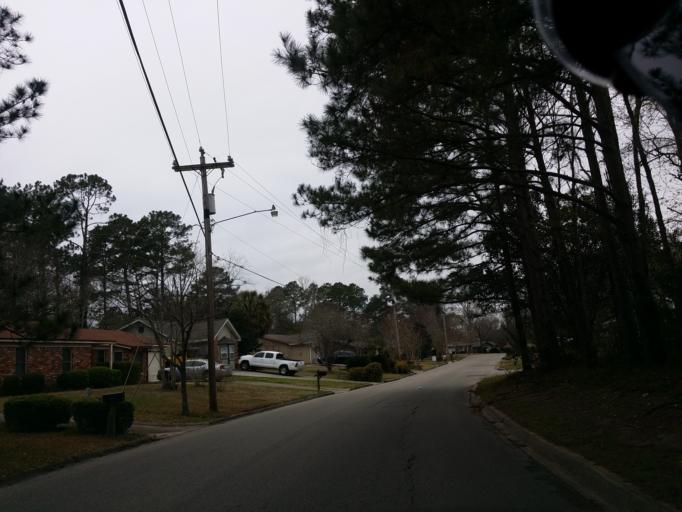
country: US
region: Florida
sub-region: Leon County
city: Tallahassee
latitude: 30.5049
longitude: -84.2236
